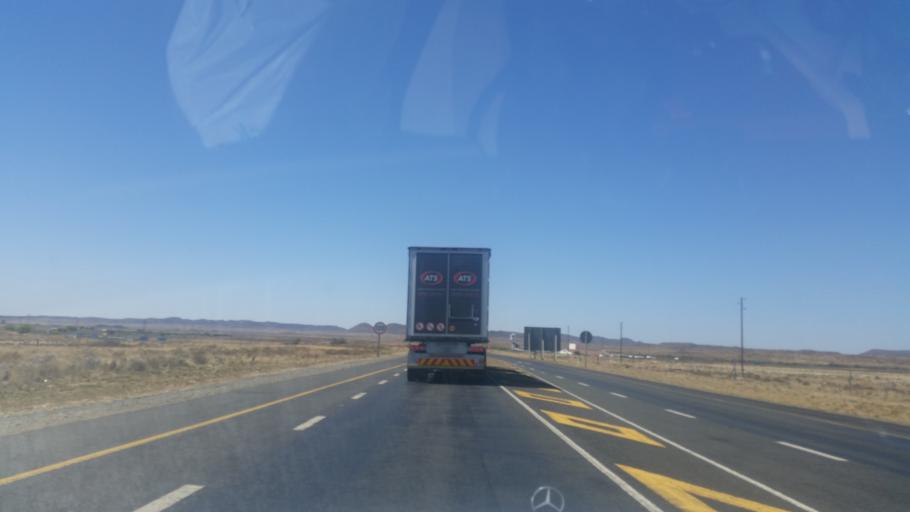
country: ZA
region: Northern Cape
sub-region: Pixley ka Seme District Municipality
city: Colesberg
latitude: -30.7029
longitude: 25.1201
